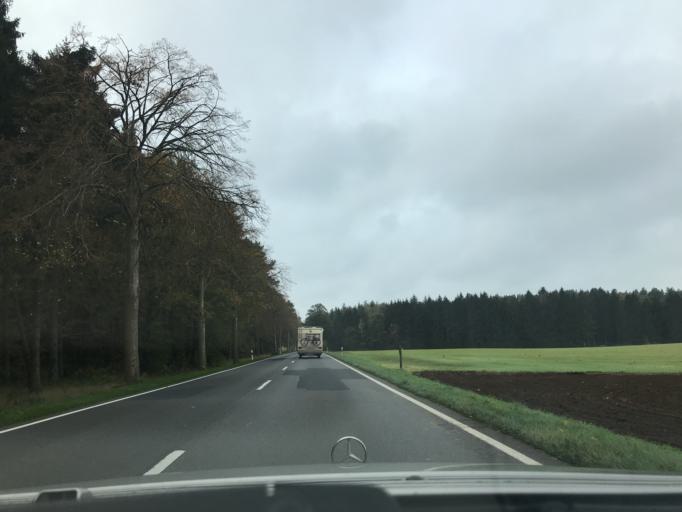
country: DE
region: Mecklenburg-Vorpommern
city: Wolgast
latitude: 54.0315
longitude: 13.6930
